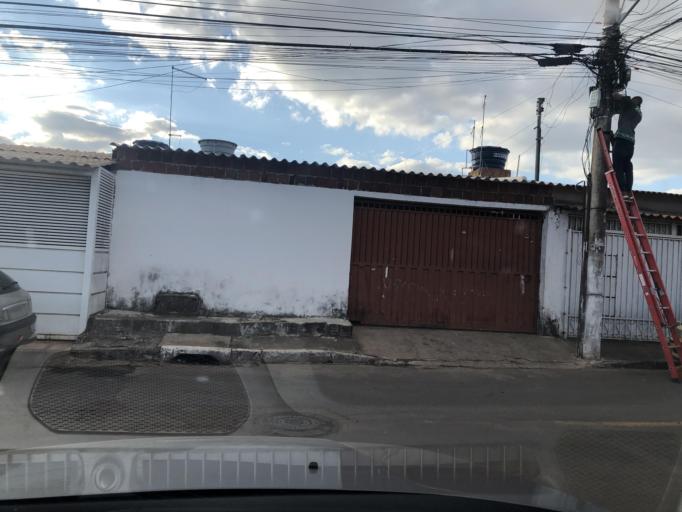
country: BR
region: Federal District
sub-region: Brasilia
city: Brasilia
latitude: -15.8697
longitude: -48.0949
